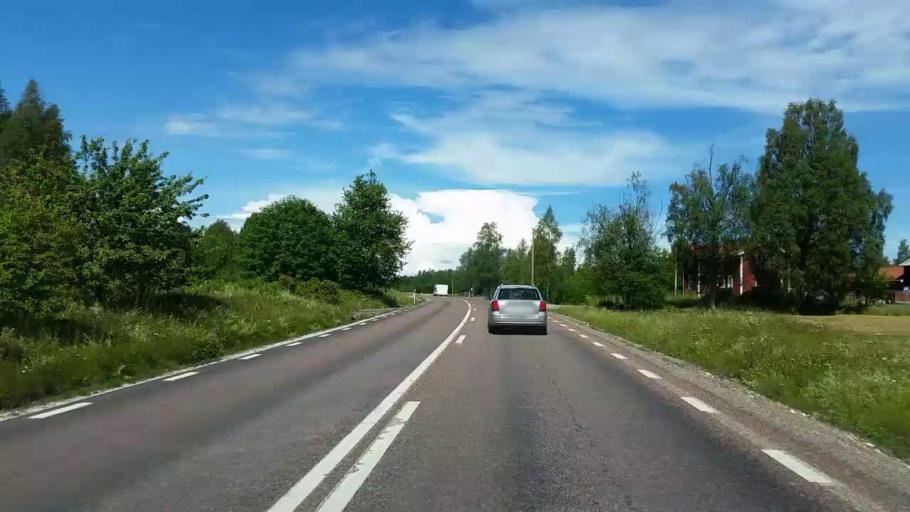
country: SE
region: Dalarna
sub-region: Rattviks Kommun
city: Raettvik
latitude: 60.9781
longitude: 15.2248
